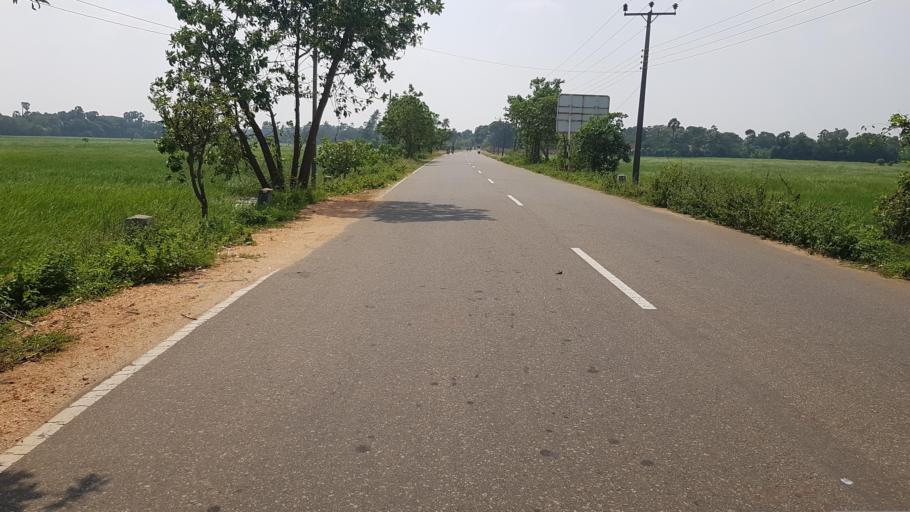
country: LK
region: Northern Province
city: Jaffna
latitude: 9.7279
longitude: 79.9484
